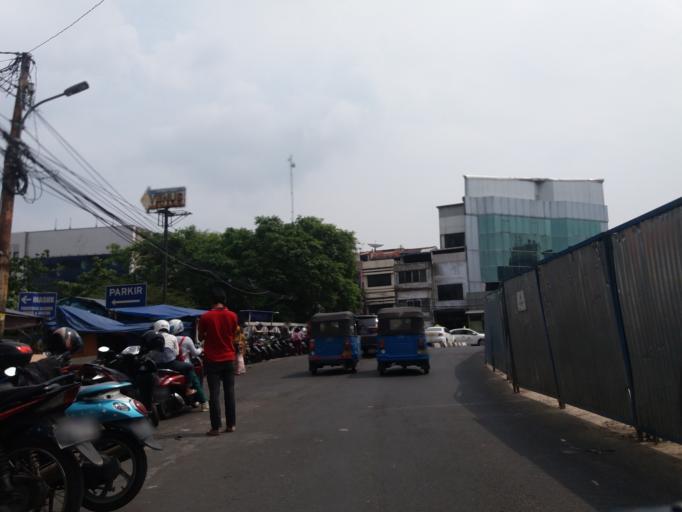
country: ID
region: Jakarta Raya
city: Jakarta
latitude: -6.1393
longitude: 106.8117
